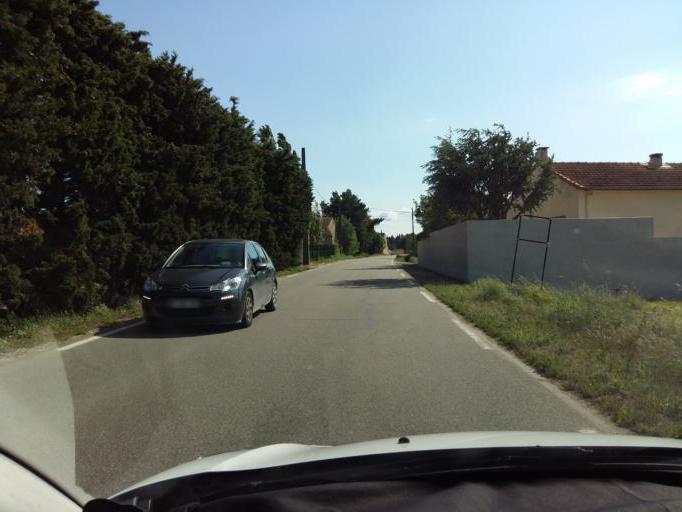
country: FR
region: Provence-Alpes-Cote d'Azur
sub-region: Departement du Vaucluse
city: Cavaillon
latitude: 43.8628
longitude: 5.0613
